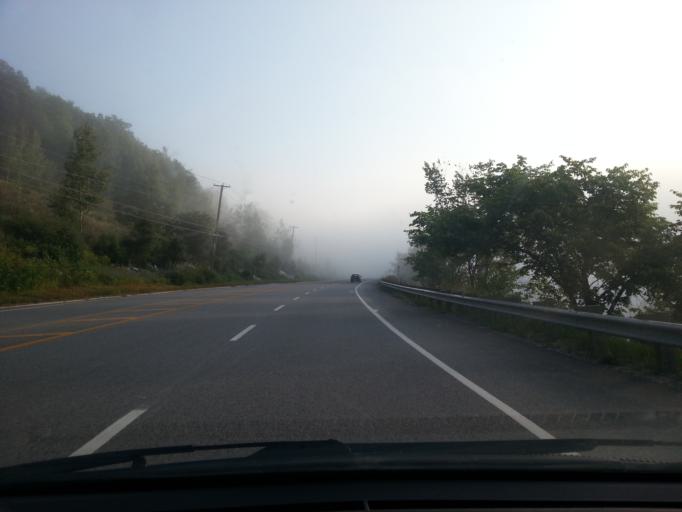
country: CA
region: Quebec
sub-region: Outaouais
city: Wakefield
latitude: 45.6997
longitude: -75.9305
